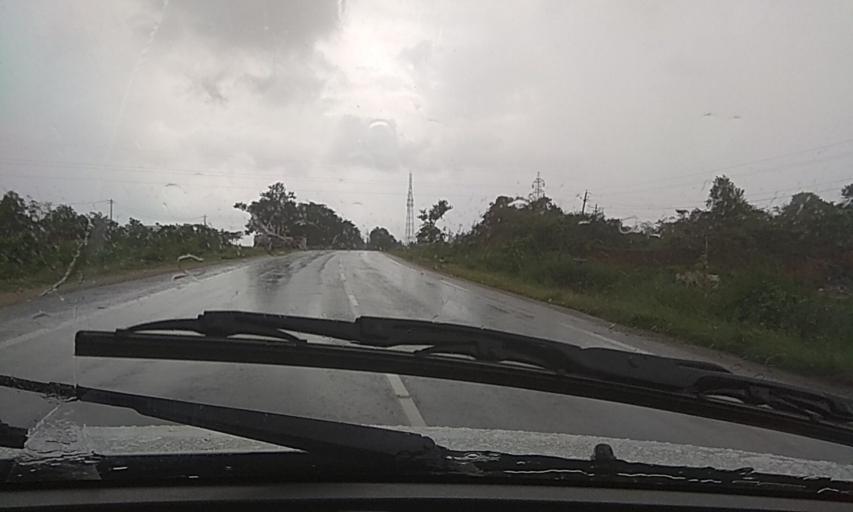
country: IN
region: Karnataka
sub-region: Tumkur
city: Kunigal
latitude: 12.9869
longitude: 77.0240
